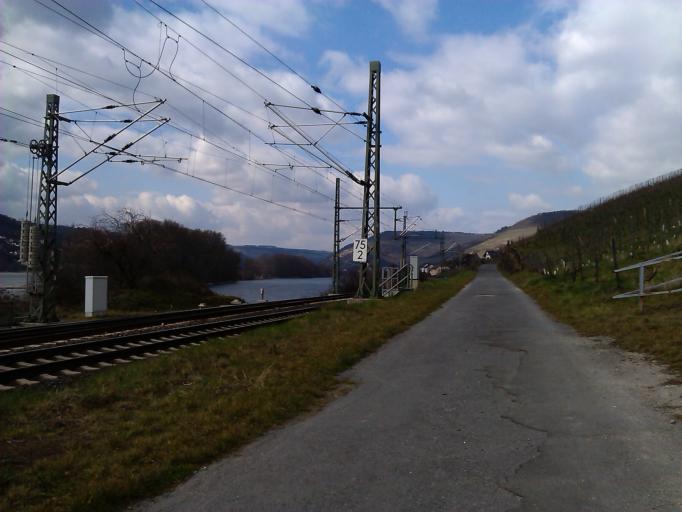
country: DE
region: Rheinland-Pfalz
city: Niederheimbach
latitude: 50.0263
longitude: 7.8295
